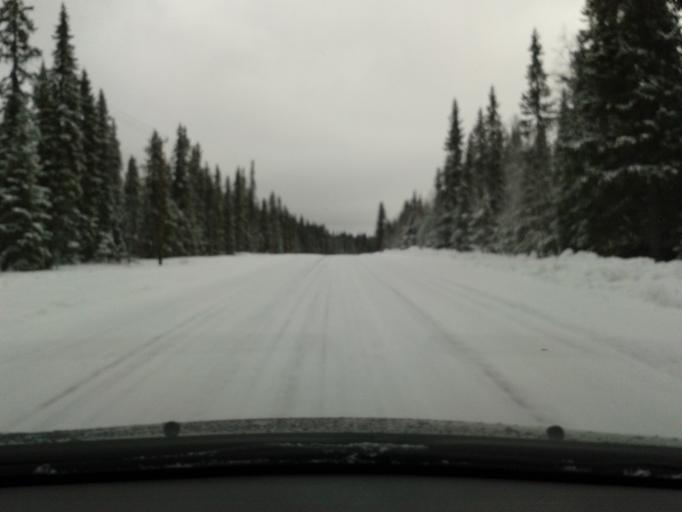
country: SE
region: Vaesterbotten
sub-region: Vilhelmina Kommun
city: Sjoberg
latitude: 65.2372
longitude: 15.8246
